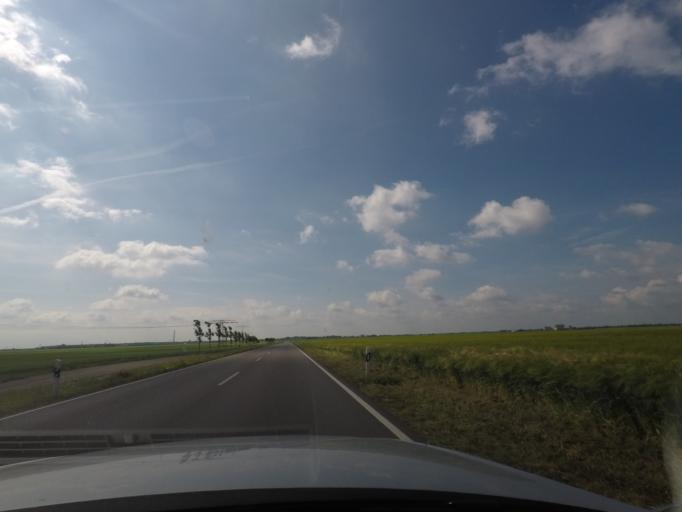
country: DE
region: Saxony
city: Markranstadt
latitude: 51.3288
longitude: 12.2063
